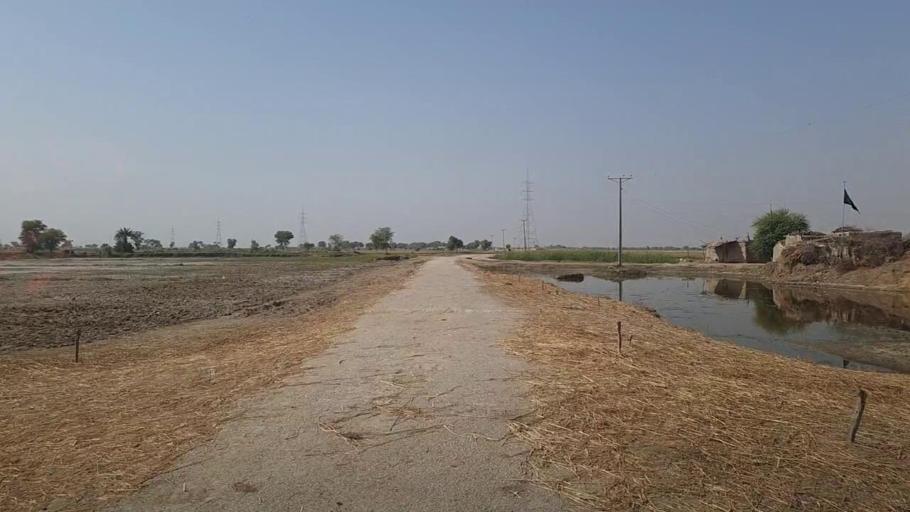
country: PK
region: Sindh
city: Kandhkot
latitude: 28.4094
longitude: 69.2471
